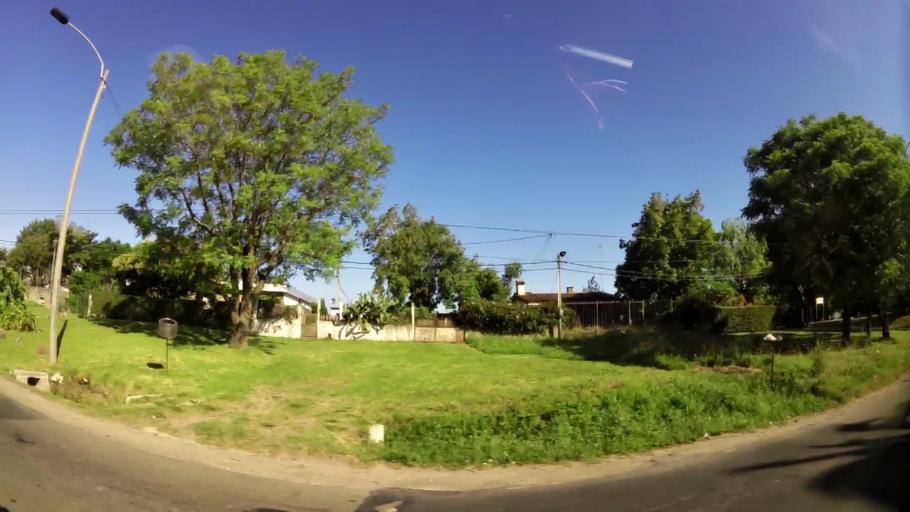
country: UY
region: Canelones
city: La Paz
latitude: -34.8080
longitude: -56.1636
